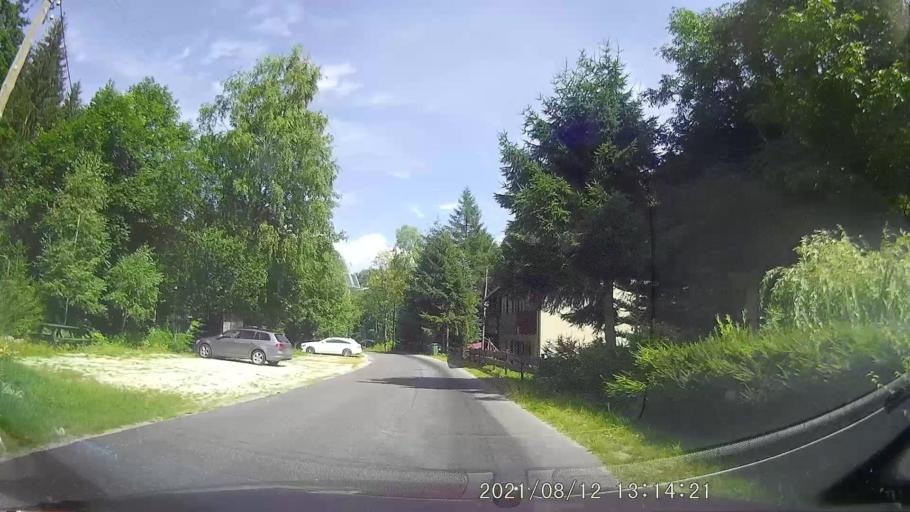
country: PL
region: Lower Silesian Voivodeship
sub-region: Powiat klodzki
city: Stronie Slaskie
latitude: 50.2583
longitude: 16.8593
